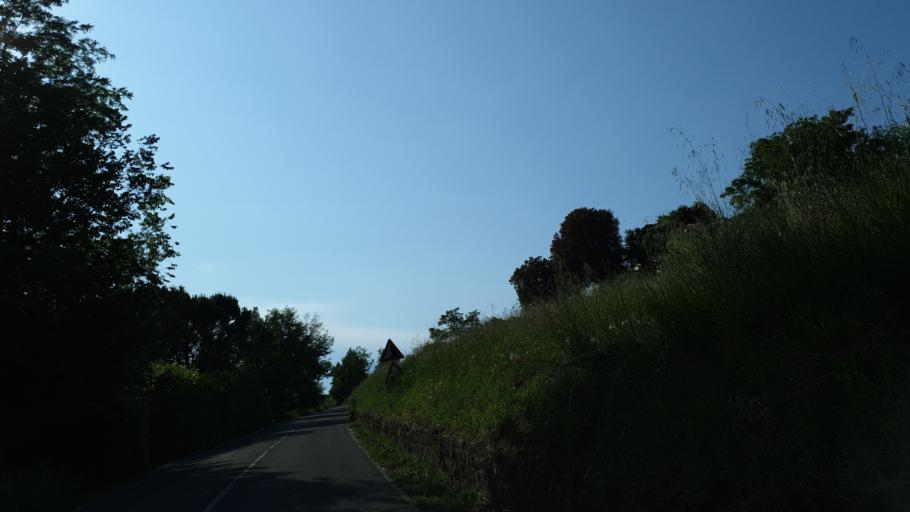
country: IT
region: Tuscany
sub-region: Province of Arezzo
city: Strada
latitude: 43.7442
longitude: 11.7328
